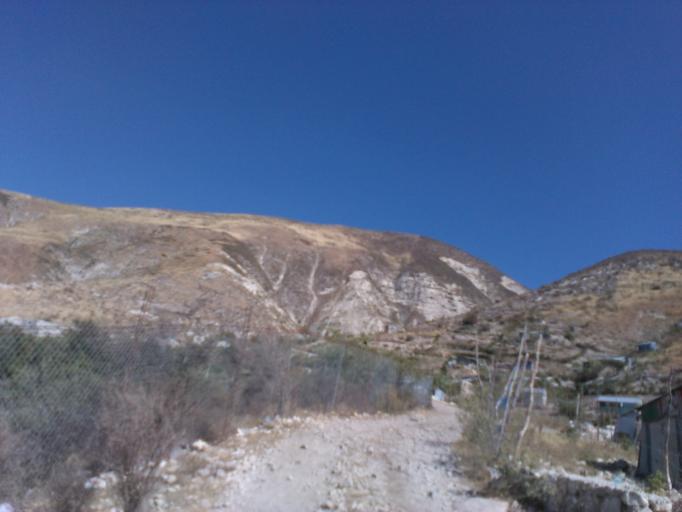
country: HT
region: Ouest
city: Croix des Bouquets
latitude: 18.6723
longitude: -72.2267
